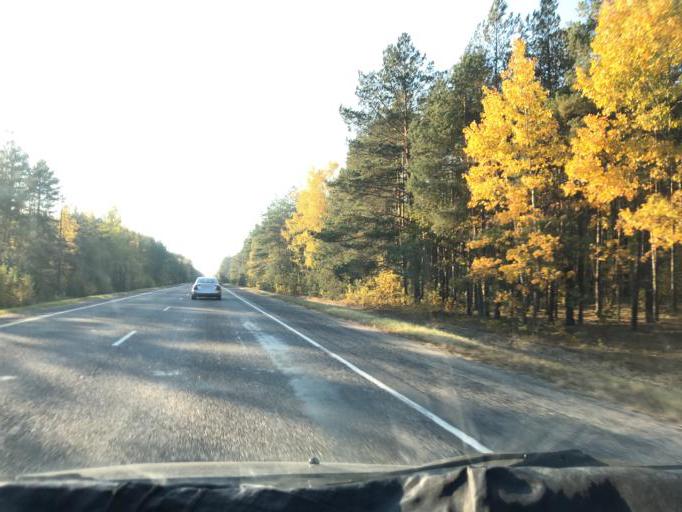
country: BY
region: Gomel
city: Zhytkavichy
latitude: 52.2726
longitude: 28.0605
